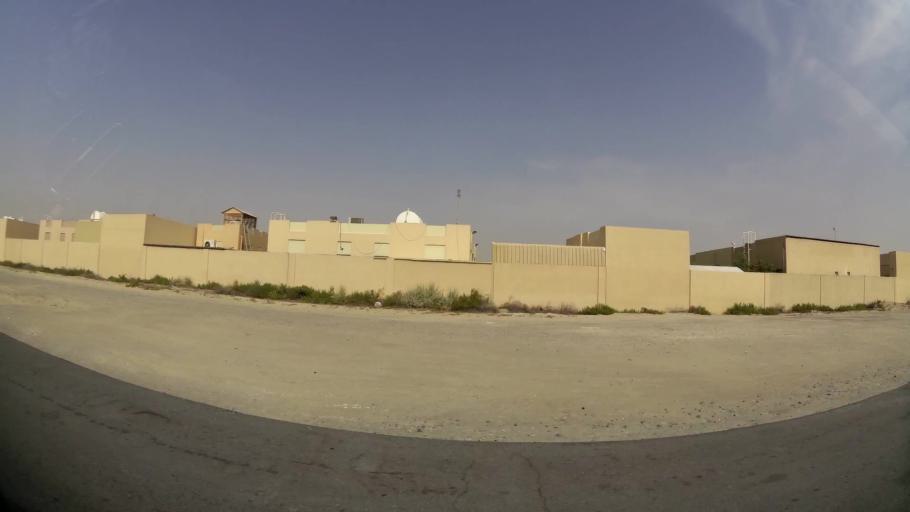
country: AE
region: Ash Shariqah
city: Sharjah
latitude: 25.2595
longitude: 55.4304
